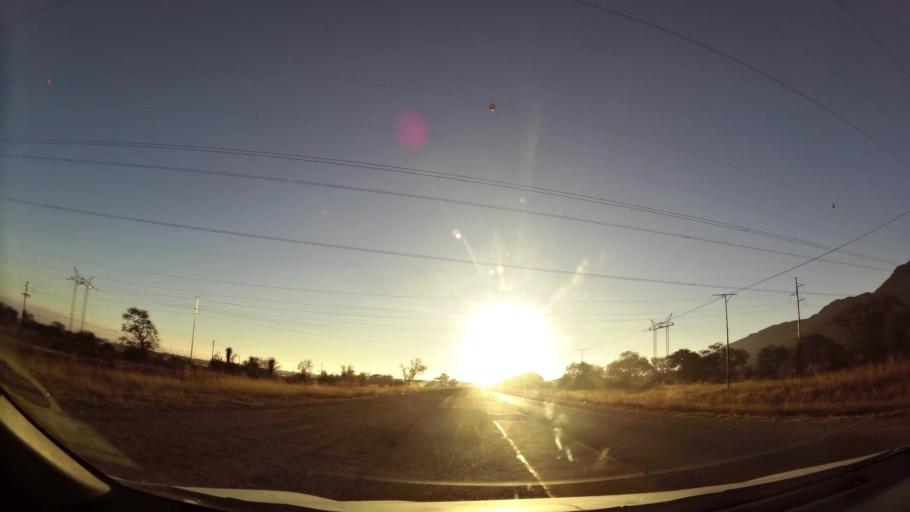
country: ZA
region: Limpopo
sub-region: Capricorn District Municipality
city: Polokwane
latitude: -24.0203
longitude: 29.3069
